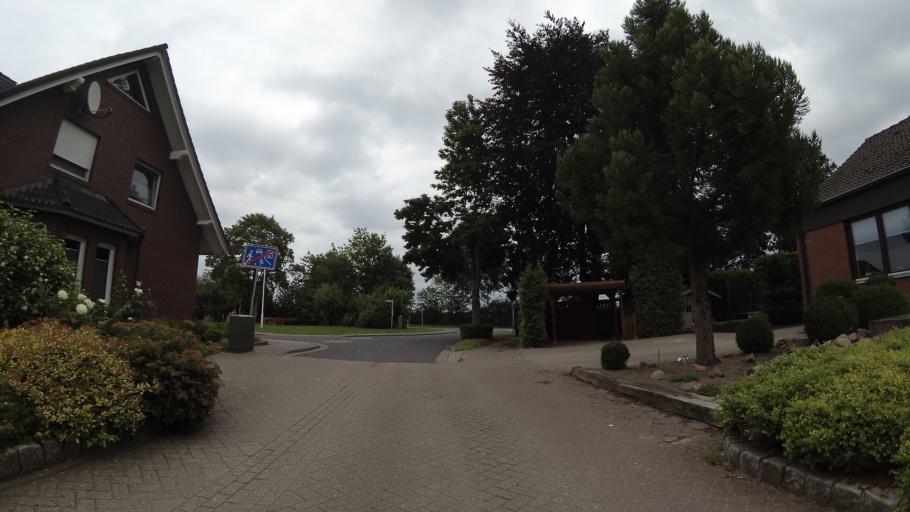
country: DE
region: Lower Saxony
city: Niederlangen
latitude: 52.8507
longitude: 7.2770
